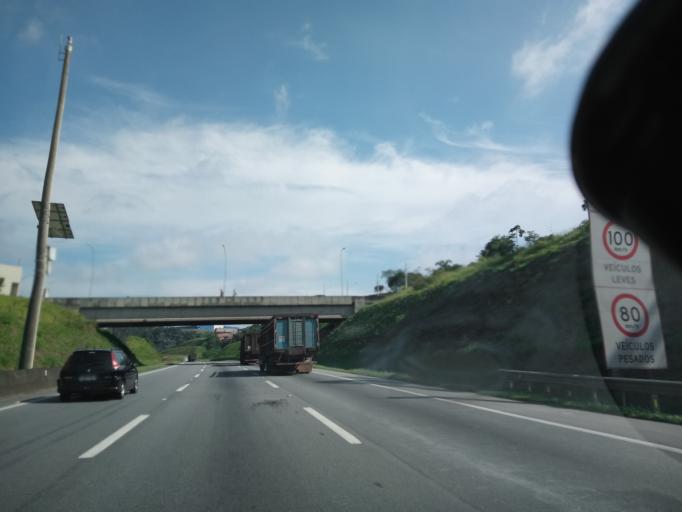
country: BR
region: Sao Paulo
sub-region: Embu
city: Embu
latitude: -23.6617
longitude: -46.8235
